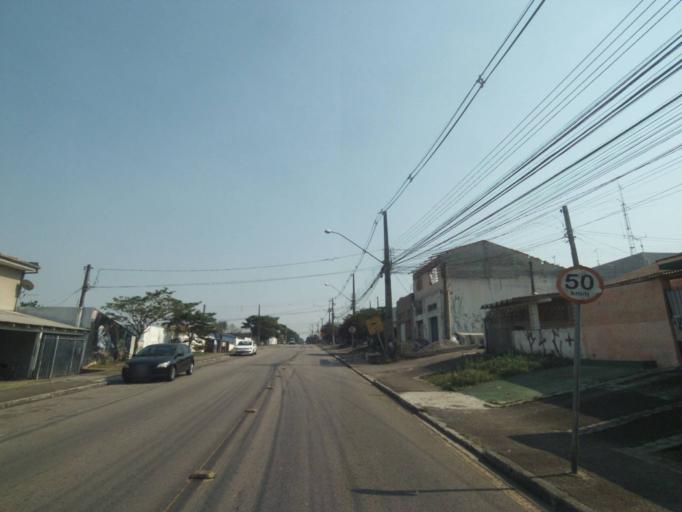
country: BR
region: Parana
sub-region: Sao Jose Dos Pinhais
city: Sao Jose dos Pinhais
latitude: -25.5223
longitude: -49.2472
